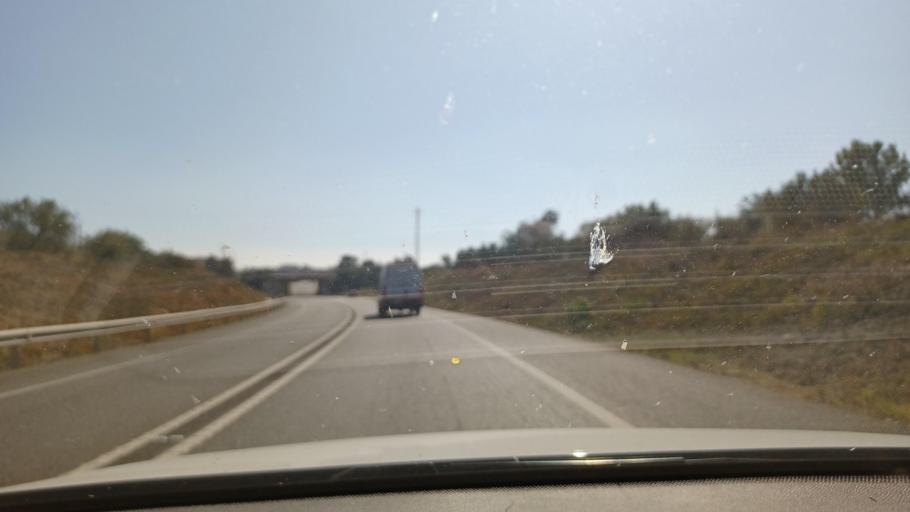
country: ES
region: Catalonia
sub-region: Provincia de Tarragona
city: L'Ampolla
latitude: 40.8149
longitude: 0.7029
